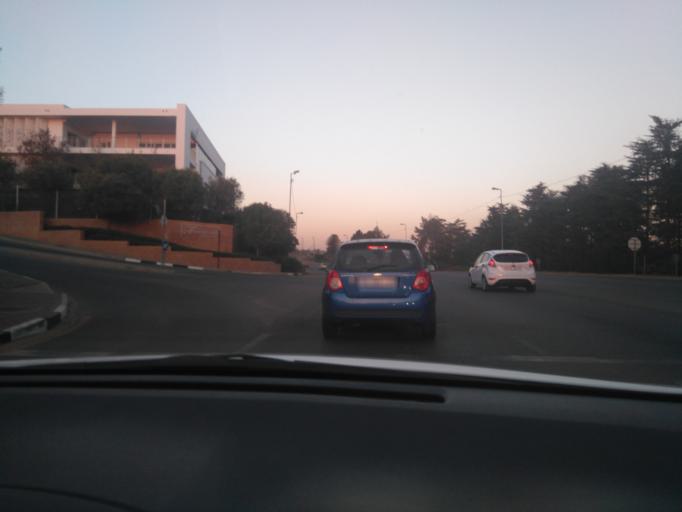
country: ZA
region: Gauteng
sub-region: City of Johannesburg Metropolitan Municipality
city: Modderfontein
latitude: -26.1009
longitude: 28.1607
